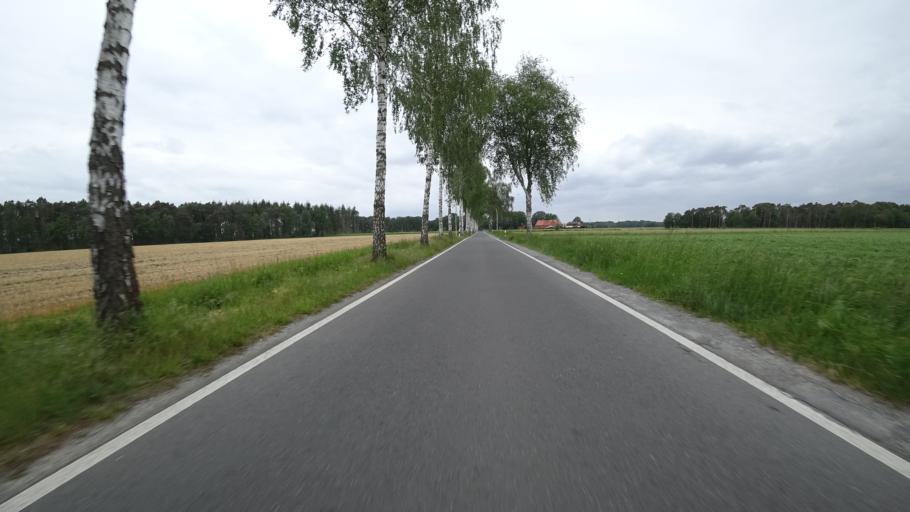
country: DE
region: North Rhine-Westphalia
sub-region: Regierungsbezirk Detmold
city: Rheda-Wiedenbruck
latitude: 51.8426
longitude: 8.3502
